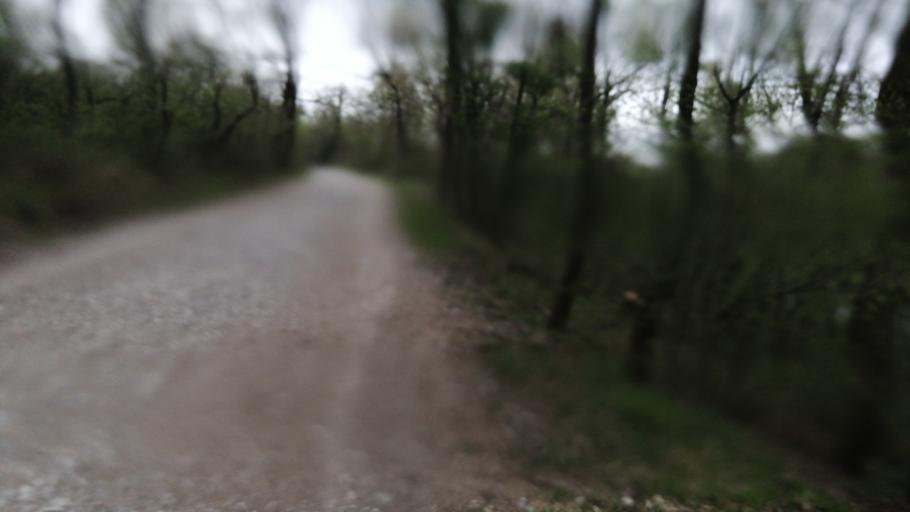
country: DE
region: Bavaria
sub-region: Upper Bavaria
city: Unterfoehring
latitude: 48.1971
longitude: 11.6374
